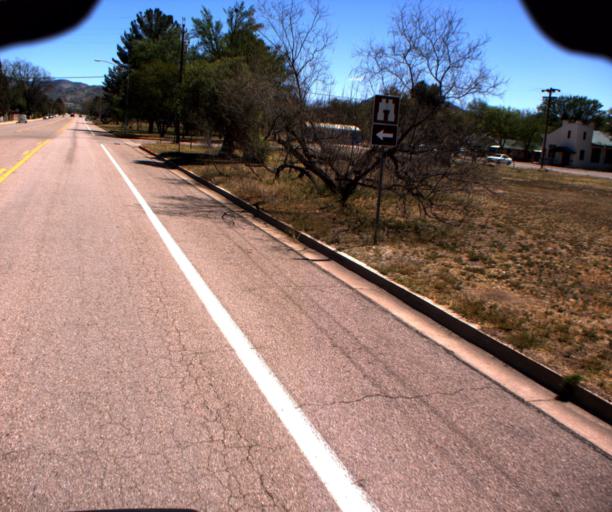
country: US
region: Arizona
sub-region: Santa Cruz County
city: Rio Rico
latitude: 31.5389
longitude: -110.7568
